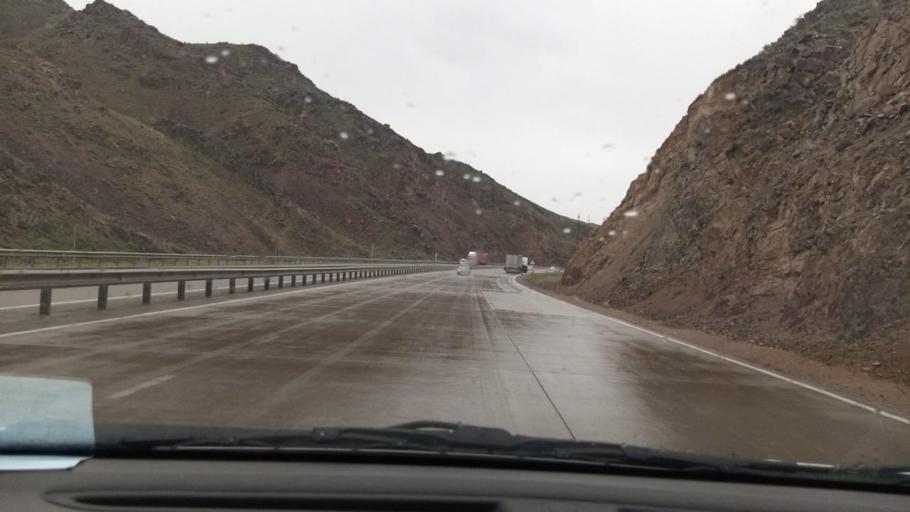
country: TJ
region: Viloyati Sughd
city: Shaydon
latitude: 40.9566
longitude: 70.6693
